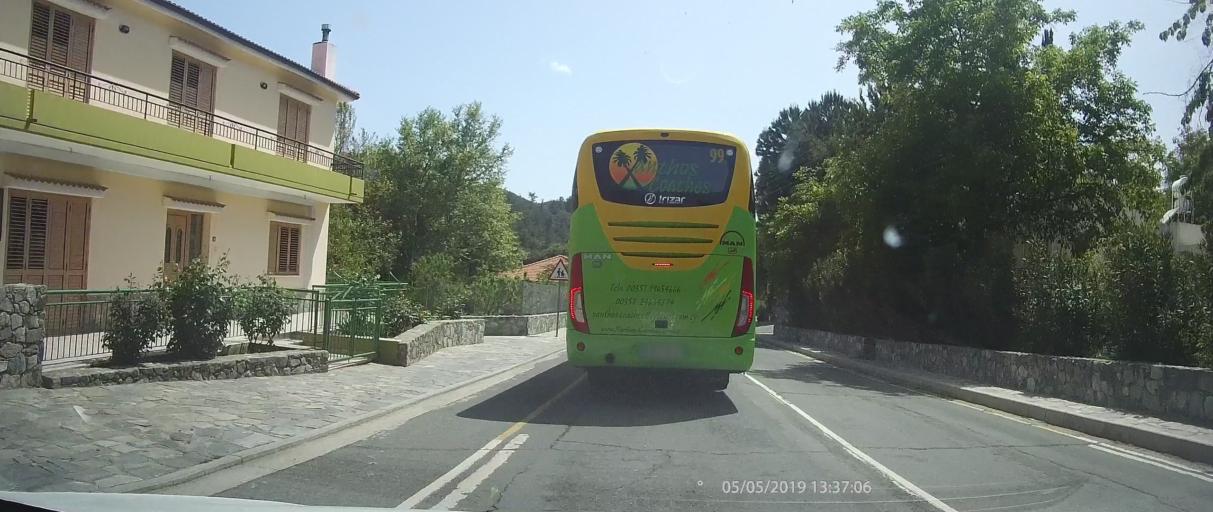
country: CY
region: Limassol
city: Pachna
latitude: 34.8786
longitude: 32.8398
